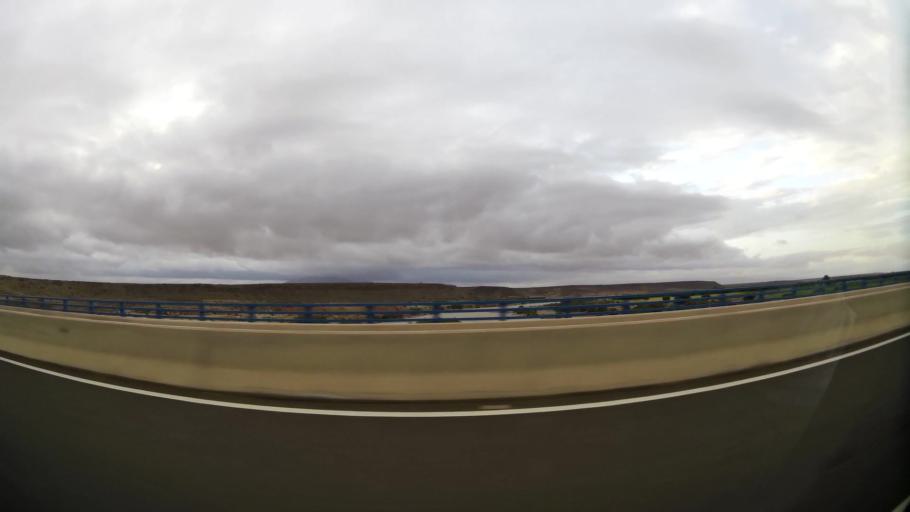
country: MA
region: Taza-Al Hoceima-Taounate
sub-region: Taza
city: Guercif
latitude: 34.3944
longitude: -3.2095
